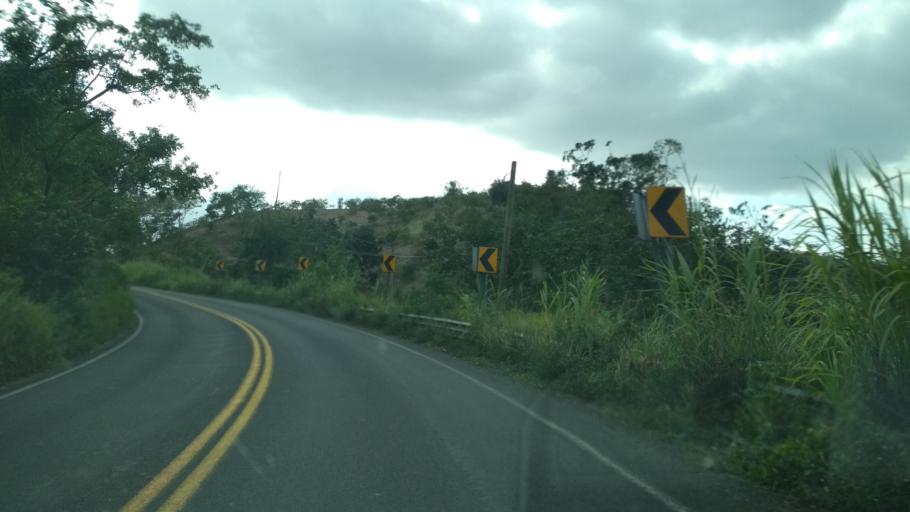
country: MX
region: Veracruz
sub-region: Papantla
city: Polutla
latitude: 20.4686
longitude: -97.2648
